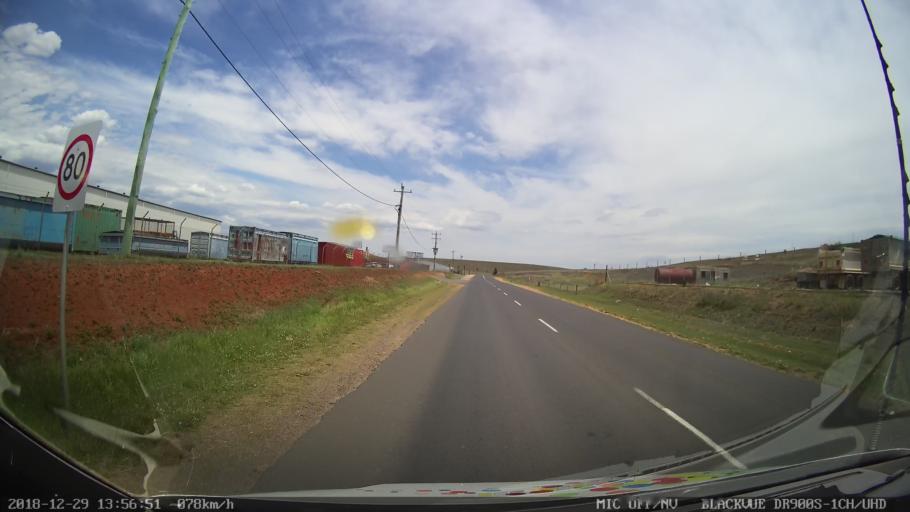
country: AU
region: New South Wales
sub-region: Cooma-Monaro
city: Cooma
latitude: -36.2349
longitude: 149.1452
